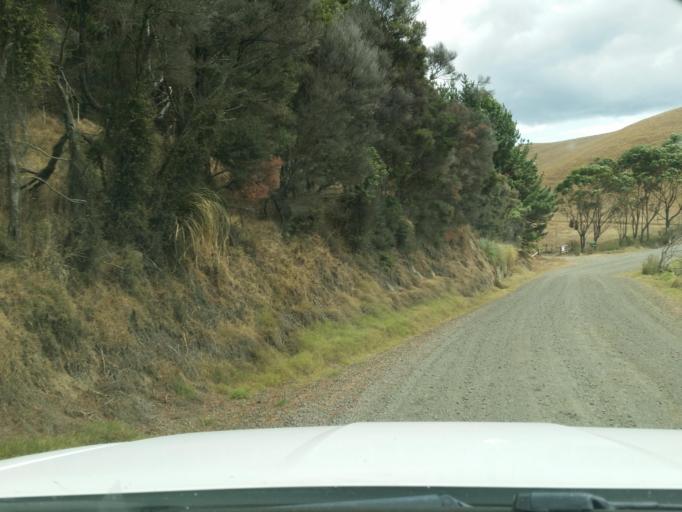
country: NZ
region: Auckland
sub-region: Auckland
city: Wellsford
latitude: -36.3357
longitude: 174.1572
